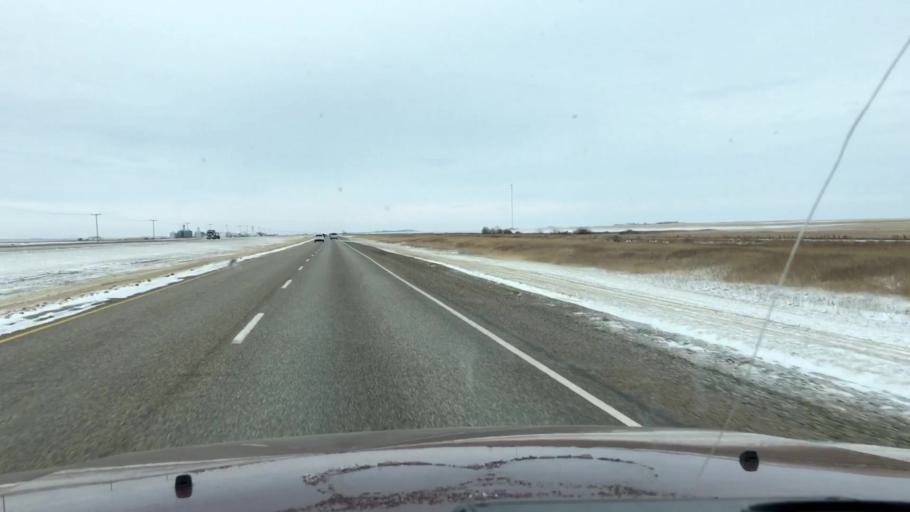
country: CA
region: Saskatchewan
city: Moose Jaw
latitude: 51.0219
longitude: -105.7882
